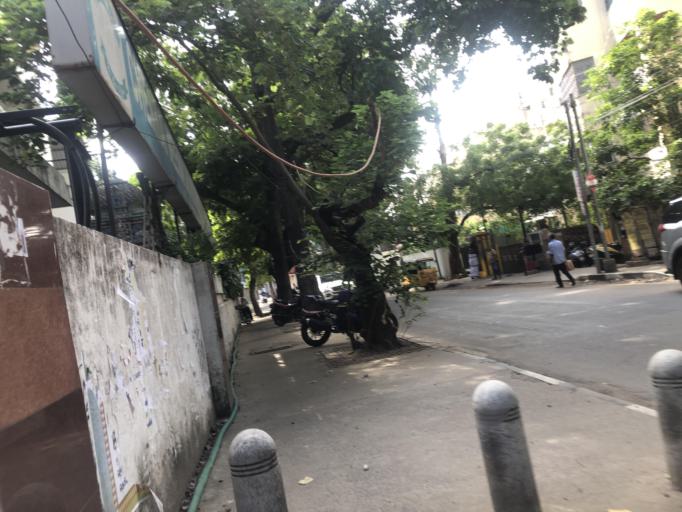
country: IN
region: Tamil Nadu
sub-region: Chennai
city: Gandhi Nagar
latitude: 13.0375
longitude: 80.2613
